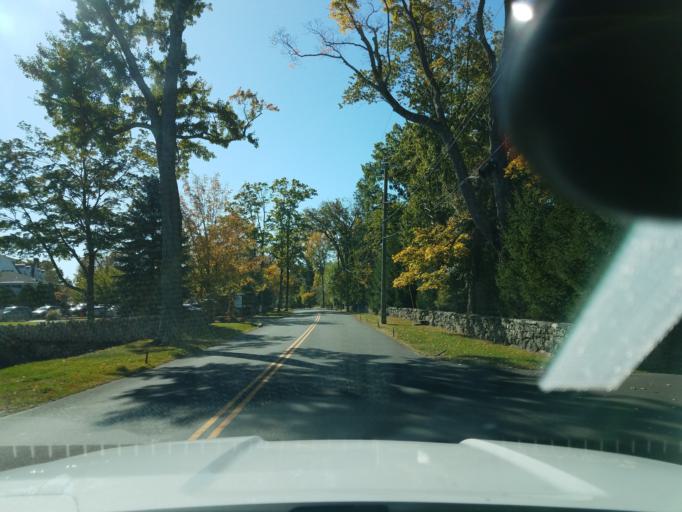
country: US
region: Connecticut
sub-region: Fairfield County
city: Cos Cob
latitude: 41.0504
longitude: -73.6163
